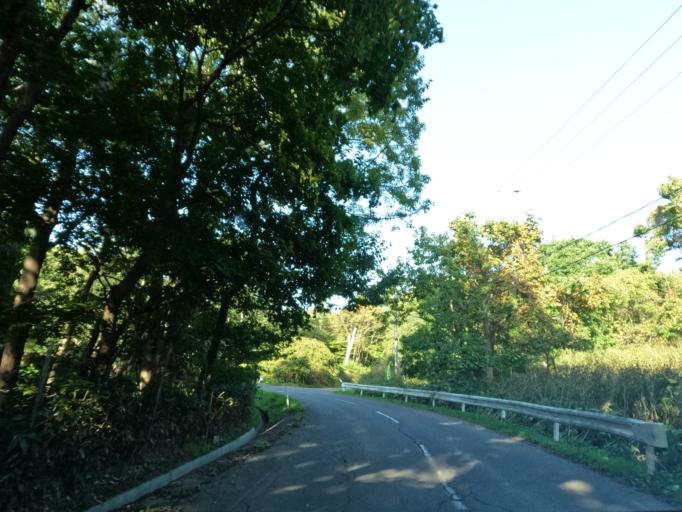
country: JP
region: Hokkaido
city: Date
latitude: 42.4021
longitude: 140.9252
